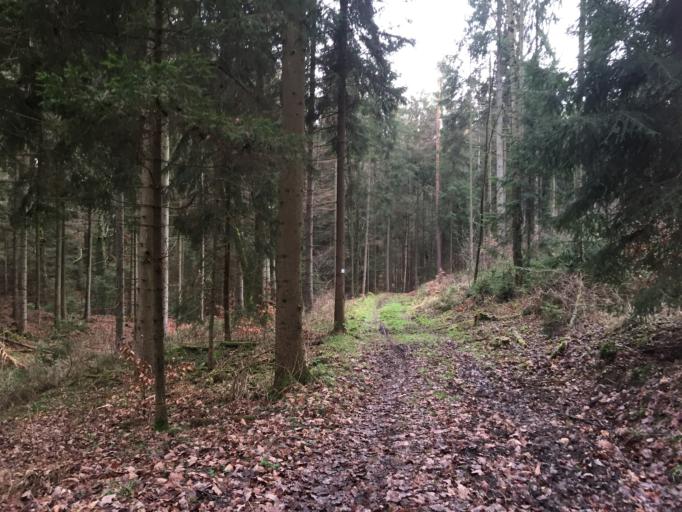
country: DE
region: Thuringia
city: Bobeck
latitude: 50.8921
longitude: 11.7919
